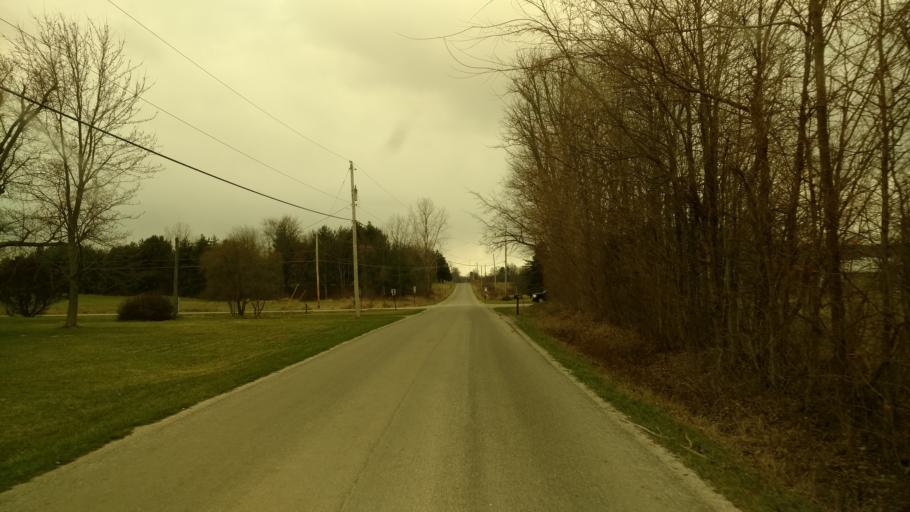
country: US
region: Ohio
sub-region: Crawford County
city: Galion
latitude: 40.6548
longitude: -82.7846
